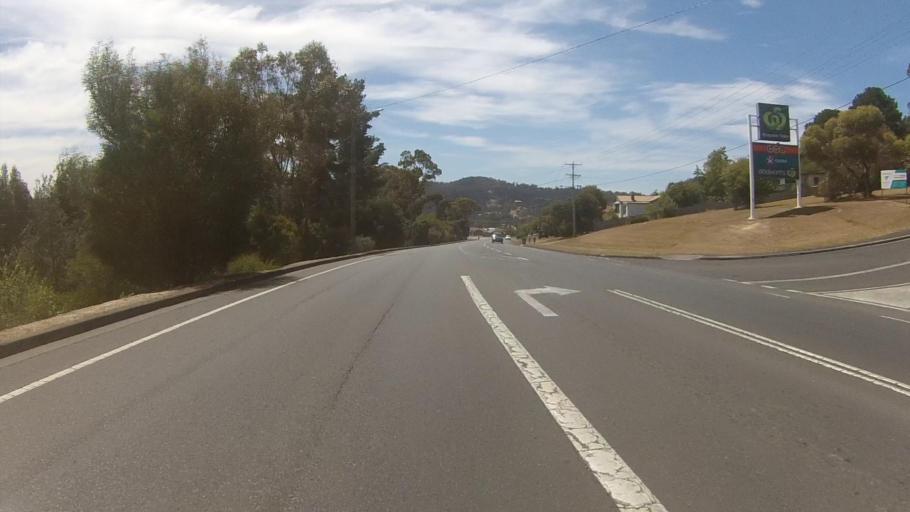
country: AU
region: Tasmania
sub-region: Kingborough
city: Kingston
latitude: -42.9790
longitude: 147.2999
